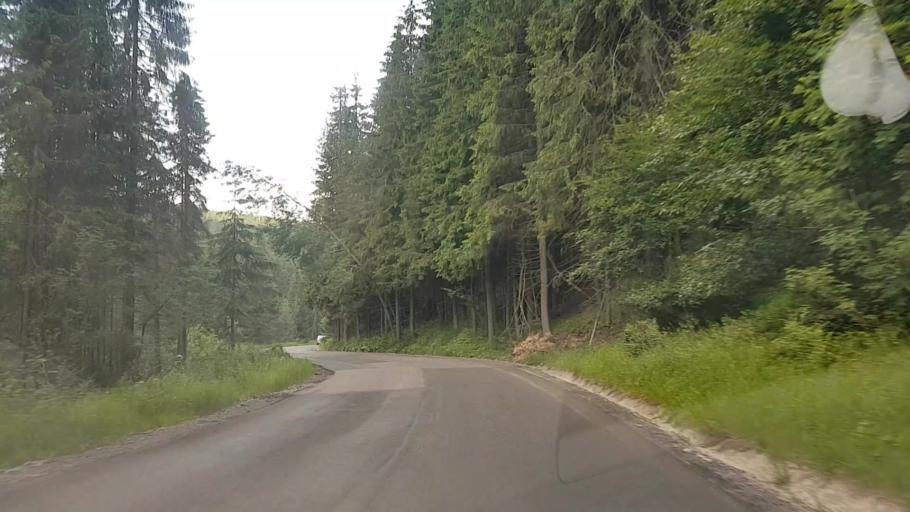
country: RO
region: Harghita
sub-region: Comuna Varsag
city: Varsag
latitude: 46.6451
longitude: 25.2866
